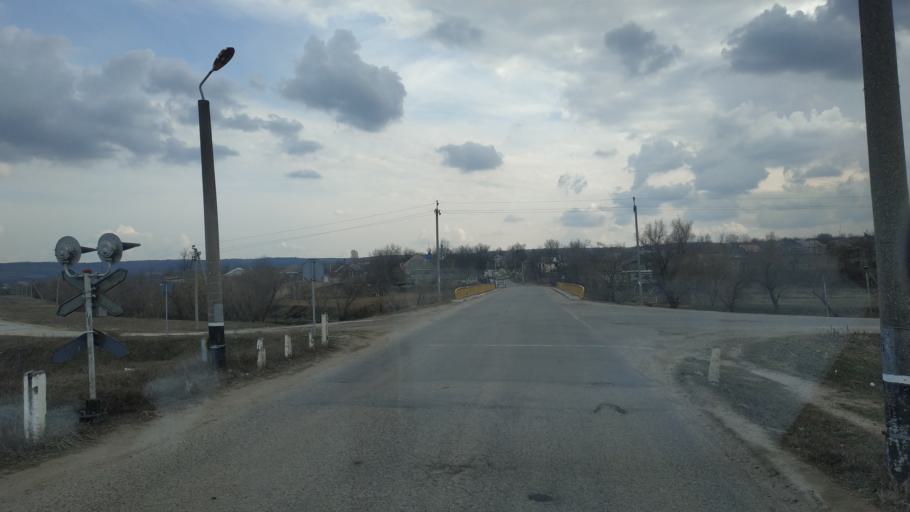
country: MD
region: Anenii Noi
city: Anenii Noi
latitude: 46.8918
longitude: 29.3020
